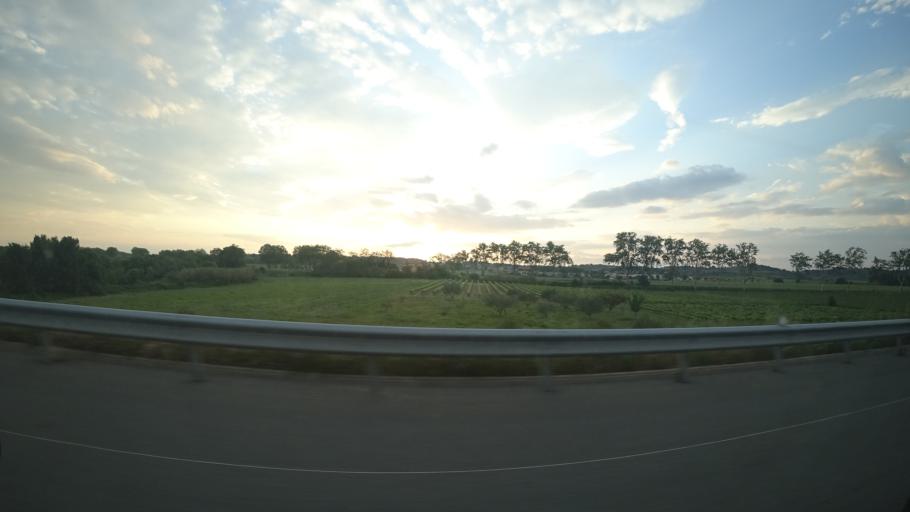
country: FR
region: Languedoc-Roussillon
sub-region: Departement de l'Herault
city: Tourbes
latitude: 43.4385
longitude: 3.3938
